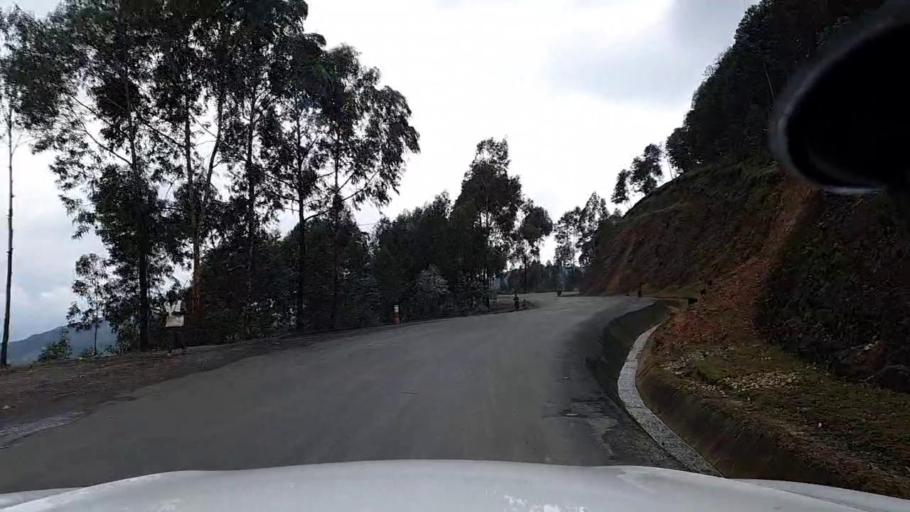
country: RW
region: Western Province
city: Kibuye
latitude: -2.0571
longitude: 29.5164
